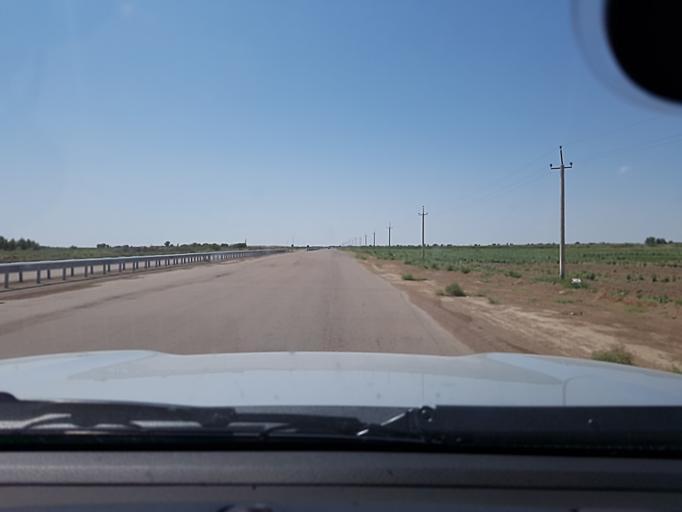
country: TM
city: Akdepe
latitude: 41.7473
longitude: 59.2570
